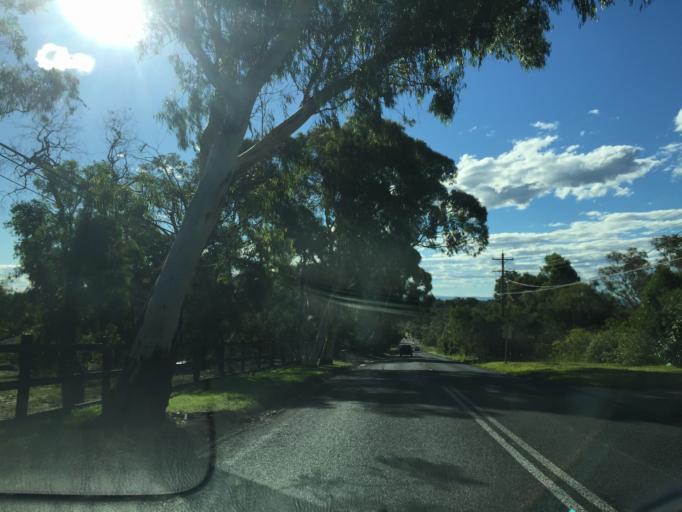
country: AU
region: New South Wales
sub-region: The Hills Shire
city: Glenhaven
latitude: -33.6955
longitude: 150.9781
